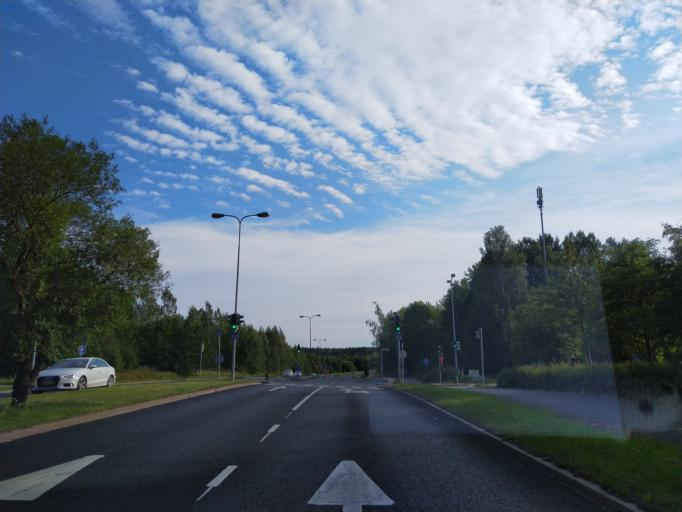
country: FI
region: Varsinais-Suomi
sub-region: Turku
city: Turku
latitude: 60.4279
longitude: 22.2400
